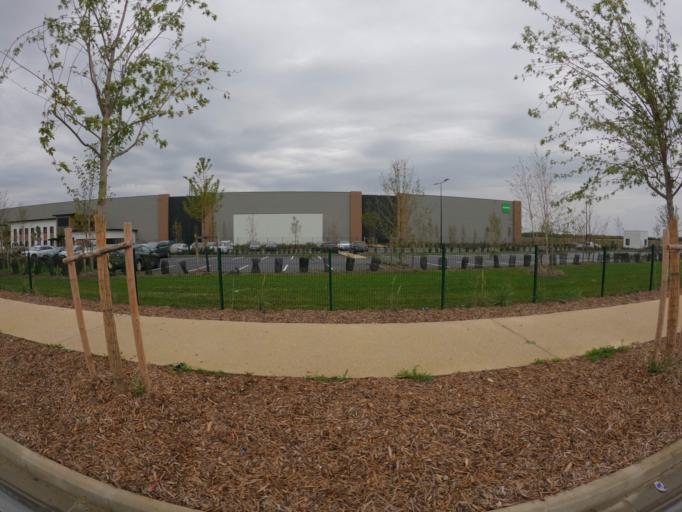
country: FR
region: Ile-de-France
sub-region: Departement de Seine-et-Marne
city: Serris
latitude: 48.8377
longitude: 2.8045
